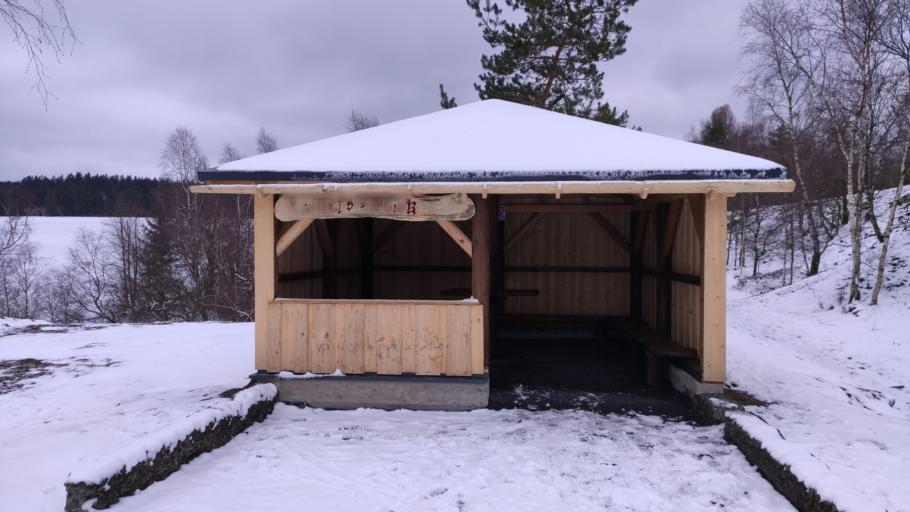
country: DE
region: Bavaria
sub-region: Upper Franconia
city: Reichenbach
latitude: 50.4702
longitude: 11.4490
